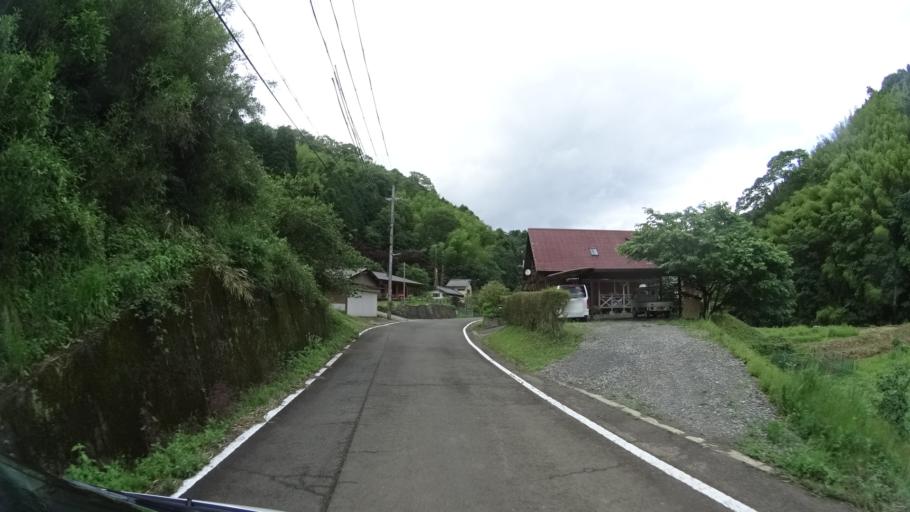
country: JP
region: Kyoto
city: Ayabe
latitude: 35.3869
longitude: 135.2107
